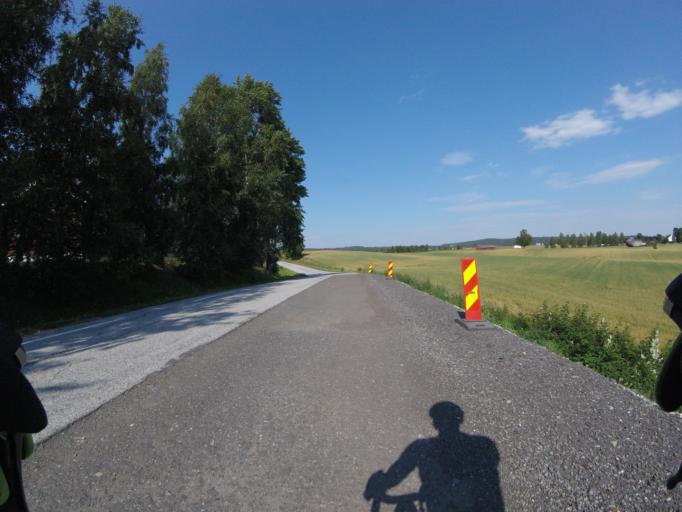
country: NO
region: Akershus
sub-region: Ullensaker
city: Klofta
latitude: 60.0945
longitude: 11.1610
